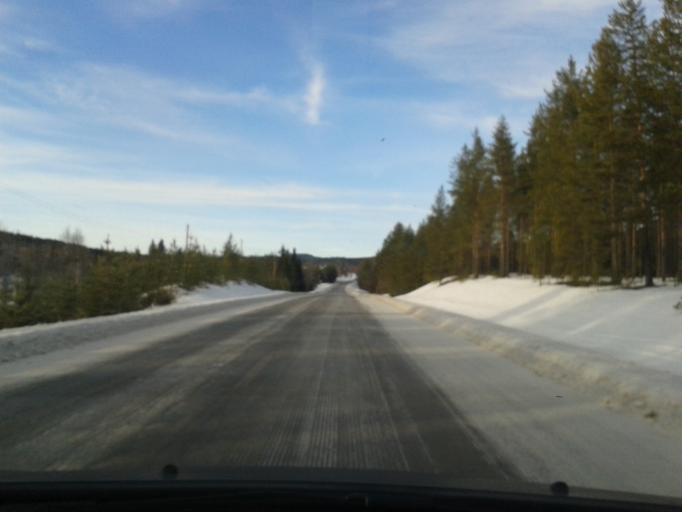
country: SE
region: Vaesternorrland
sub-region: OErnskoeldsviks Kommun
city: Bredbyn
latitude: 63.5623
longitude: 17.9375
